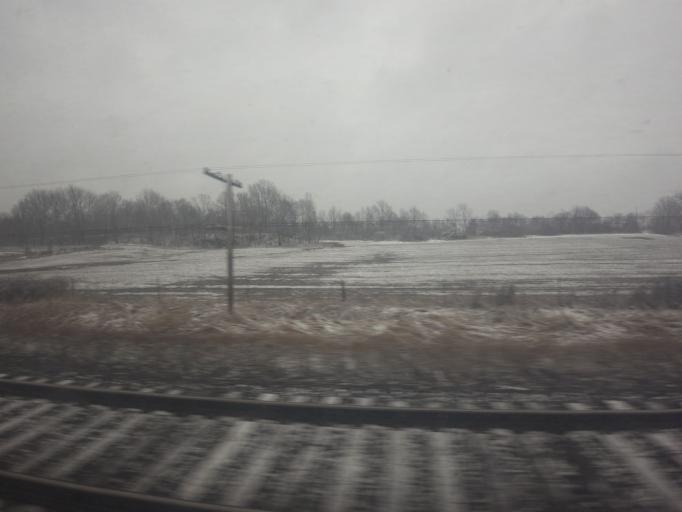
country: US
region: New York
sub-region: Jefferson County
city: Alexandria Bay
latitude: 44.4923
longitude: -75.8714
